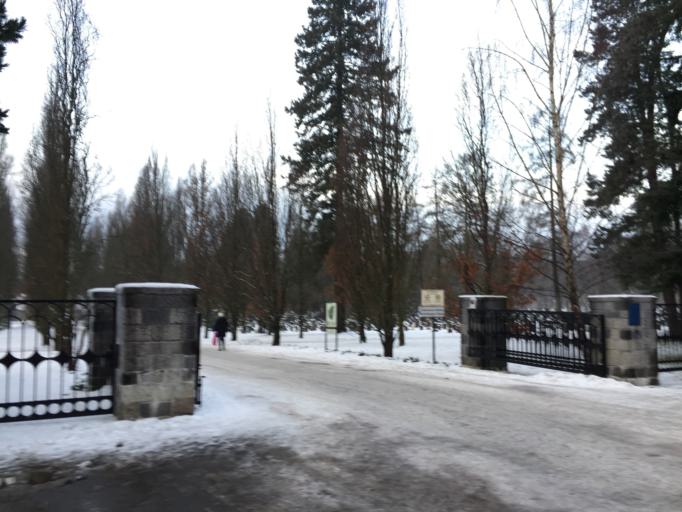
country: NO
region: Oslo
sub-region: Oslo
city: Sjolyststranda
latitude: 59.9305
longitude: 10.6999
